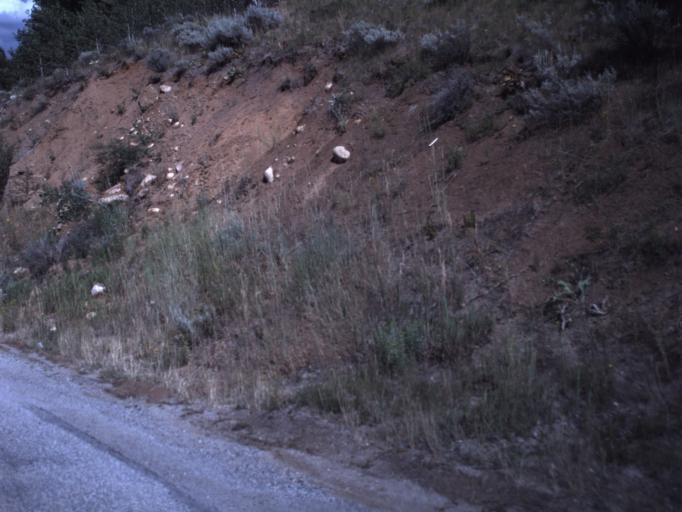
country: US
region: Utah
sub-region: Cache County
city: North Logan
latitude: 41.8311
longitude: -111.6038
